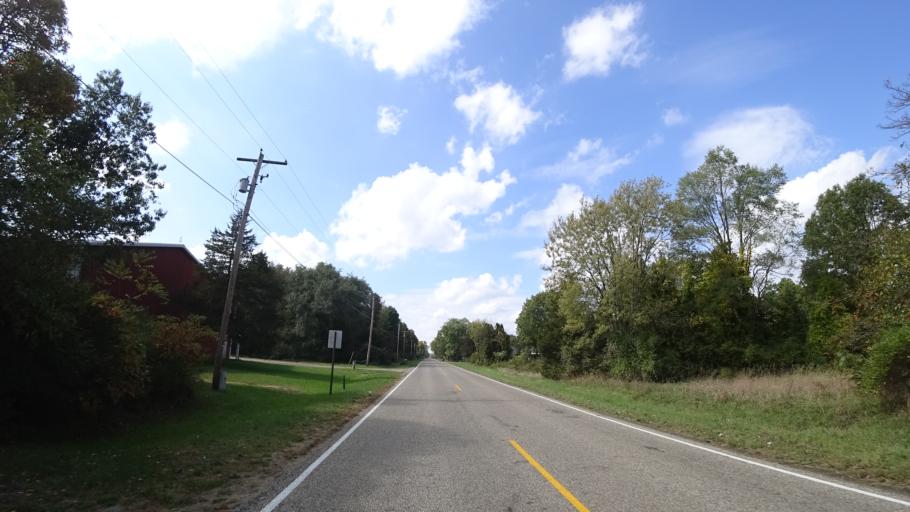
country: US
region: Michigan
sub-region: Saint Joseph County
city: Three Rivers
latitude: 41.9401
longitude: -85.6104
